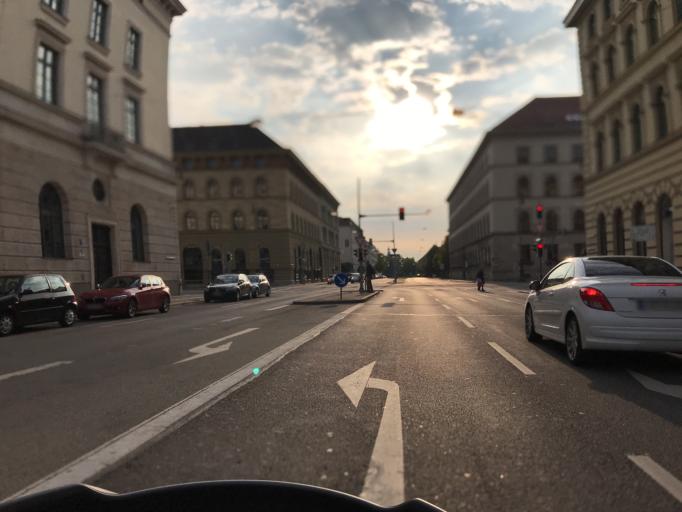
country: DE
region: Bavaria
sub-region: Upper Bavaria
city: Munich
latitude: 48.1454
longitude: 11.5779
